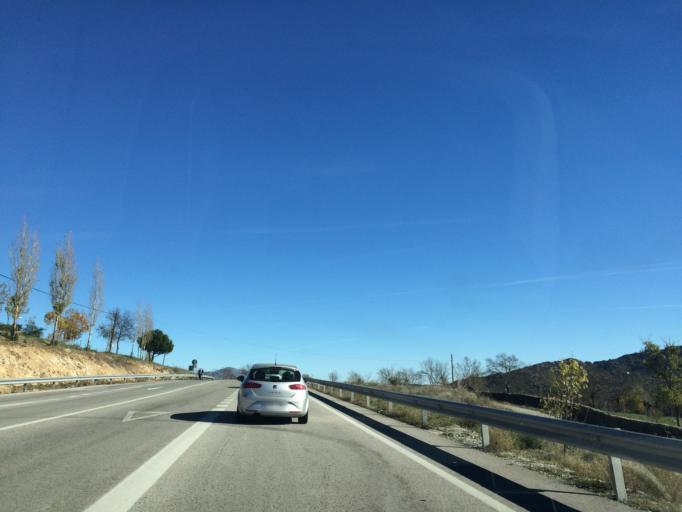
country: ES
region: Madrid
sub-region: Provincia de Madrid
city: Manzanares el Real
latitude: 40.7240
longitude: -3.8745
